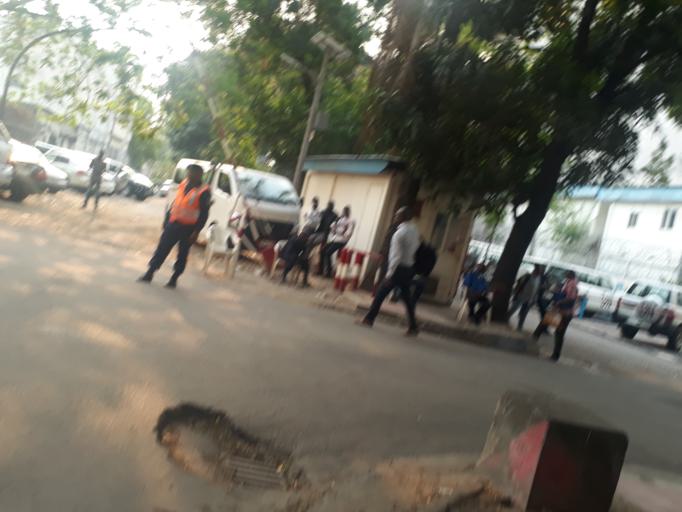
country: CD
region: Kinshasa
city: Kinshasa
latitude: -4.3006
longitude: 15.3123
